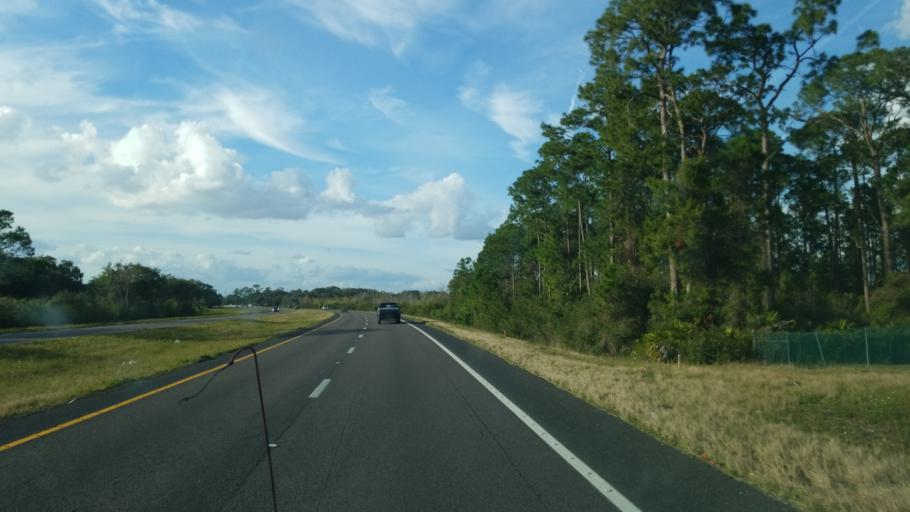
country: US
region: Florida
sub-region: Osceola County
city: Saint Cloud
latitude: 28.2296
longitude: -81.1846
